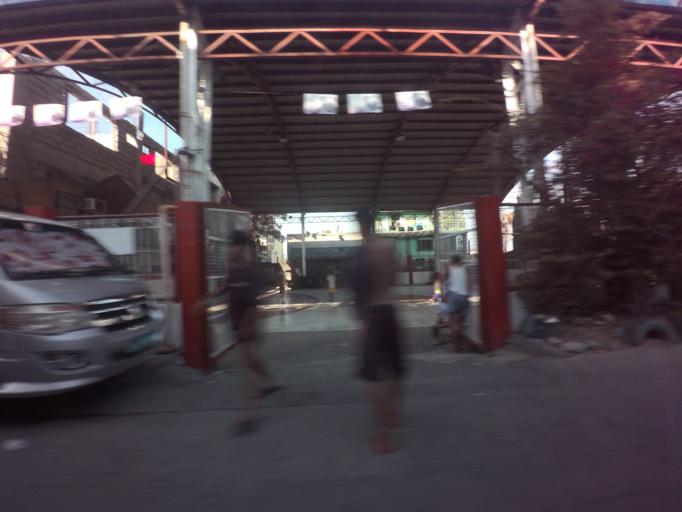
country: PH
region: Calabarzon
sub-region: Province of Rizal
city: Taguig
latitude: 14.4953
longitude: 121.0479
